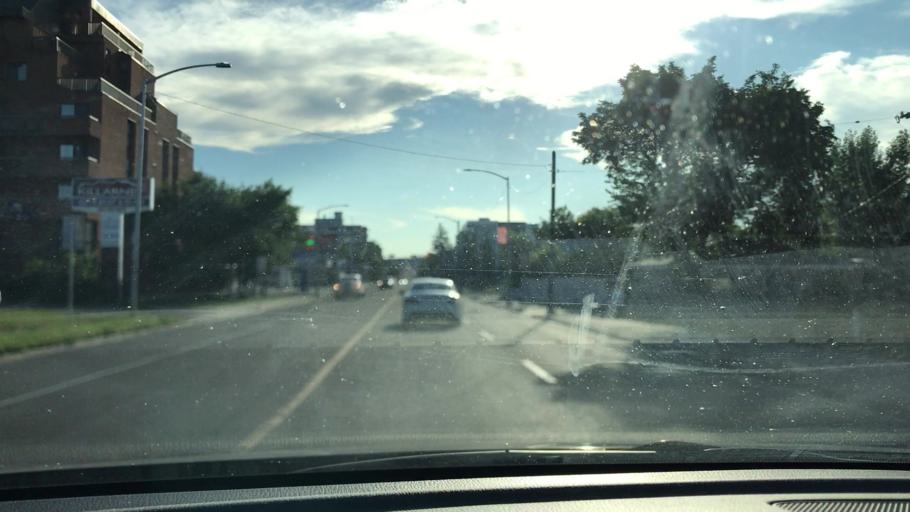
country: CA
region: Alberta
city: Calgary
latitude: 51.0378
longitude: -114.1210
